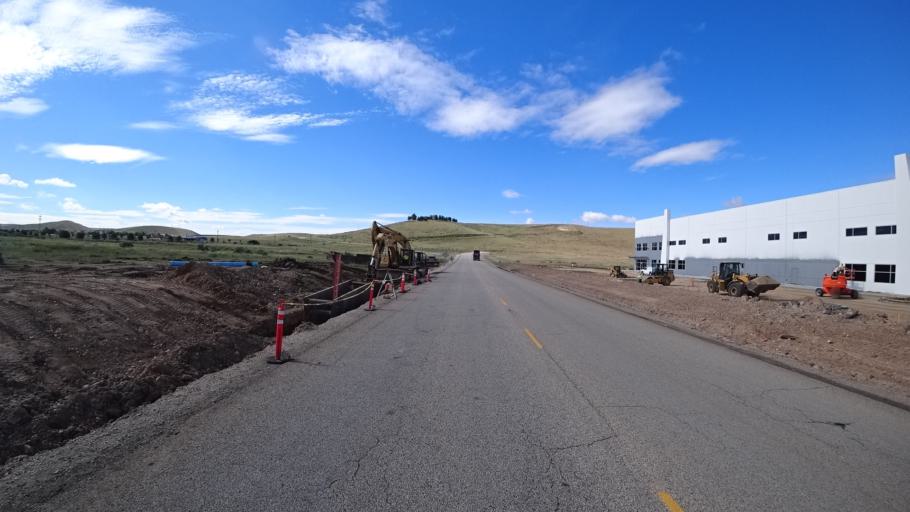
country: US
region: Idaho
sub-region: Ada County
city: Boise
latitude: 43.5155
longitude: -116.1514
